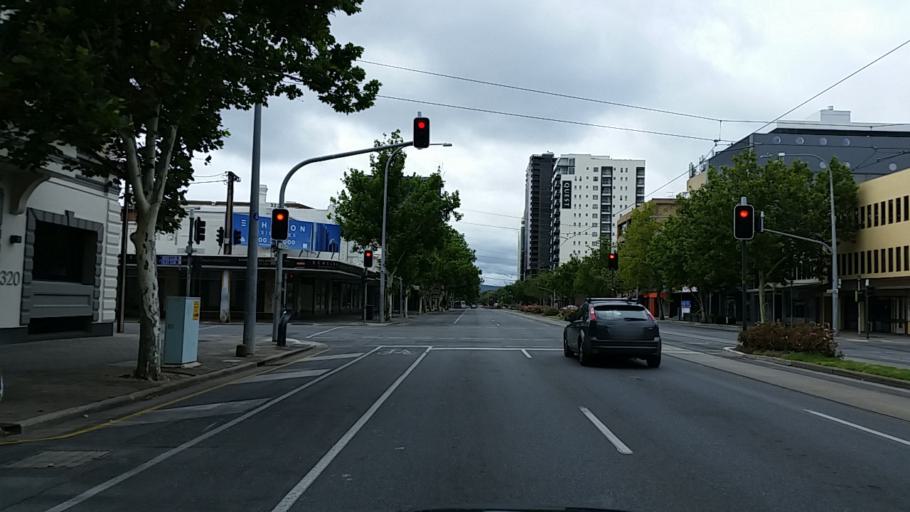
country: AU
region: South Australia
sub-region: Adelaide
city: Adelaide
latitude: -34.9312
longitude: 138.6002
